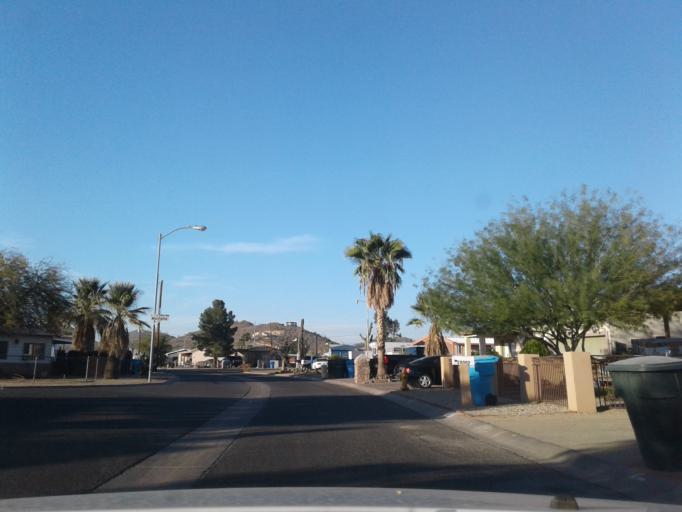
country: US
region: Arizona
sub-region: Maricopa County
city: Paradise Valley
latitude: 33.6496
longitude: -112.0356
